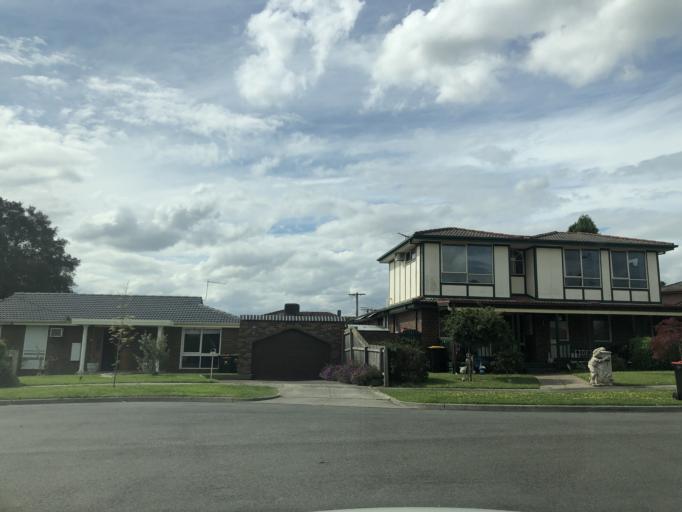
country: AU
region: Victoria
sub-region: Greater Dandenong
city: Noble Park North
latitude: -37.9525
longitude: 145.1985
